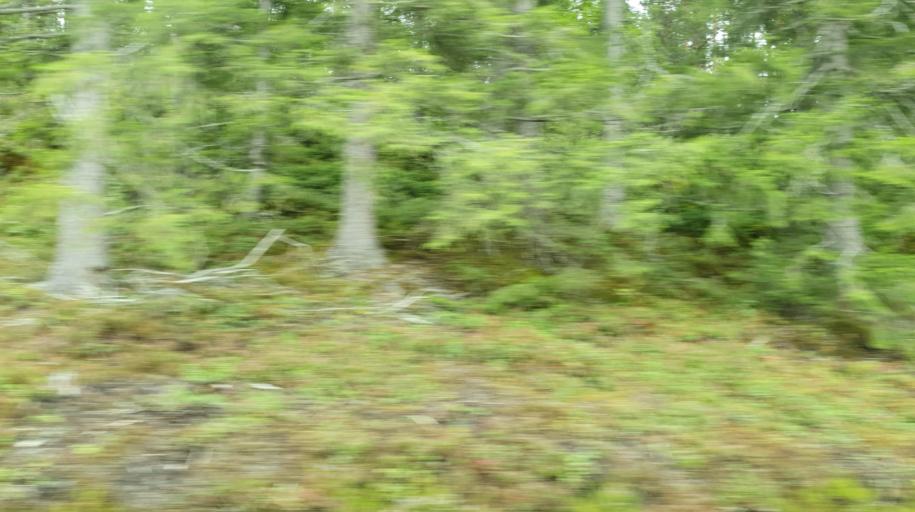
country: NO
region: Nord-Trondelag
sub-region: Stjordal
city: Stjordalshalsen
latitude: 63.3990
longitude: 10.9690
